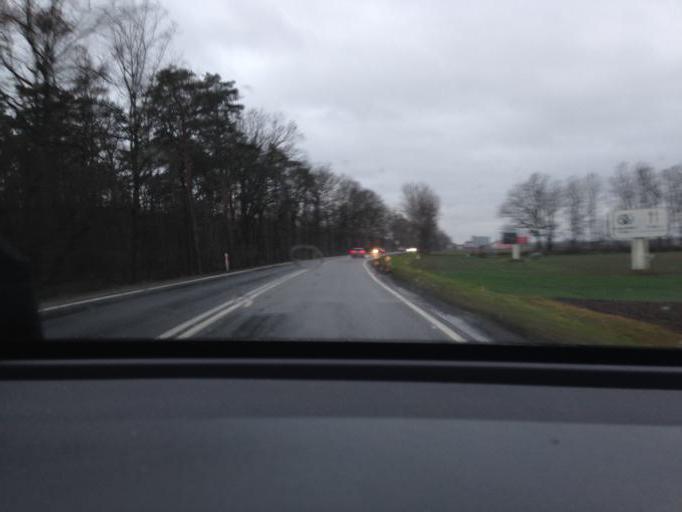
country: PL
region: Opole Voivodeship
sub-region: Powiat opolski
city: Wegry
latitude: 50.7060
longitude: 17.9827
